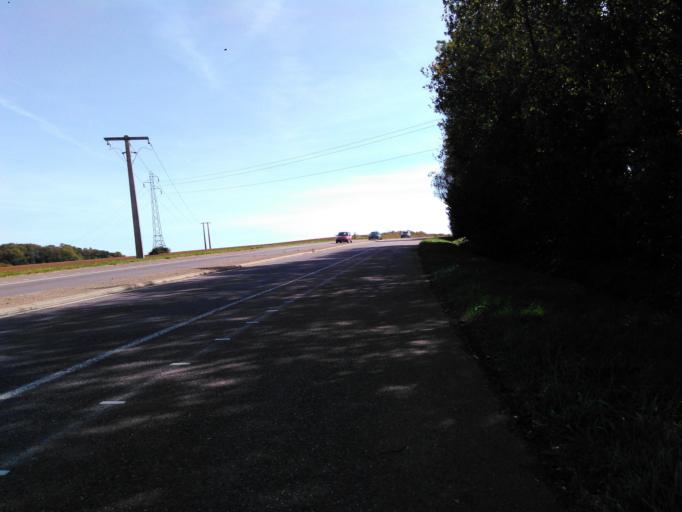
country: FR
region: Lorraine
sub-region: Departement de la Moselle
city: Hettange-Grande
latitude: 49.3921
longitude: 6.1675
